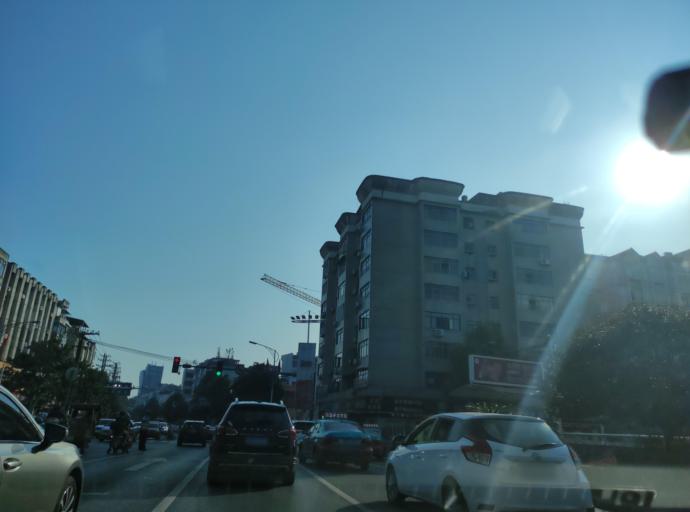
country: CN
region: Jiangxi Sheng
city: Pingxiang
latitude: 27.6300
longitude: 113.8508
